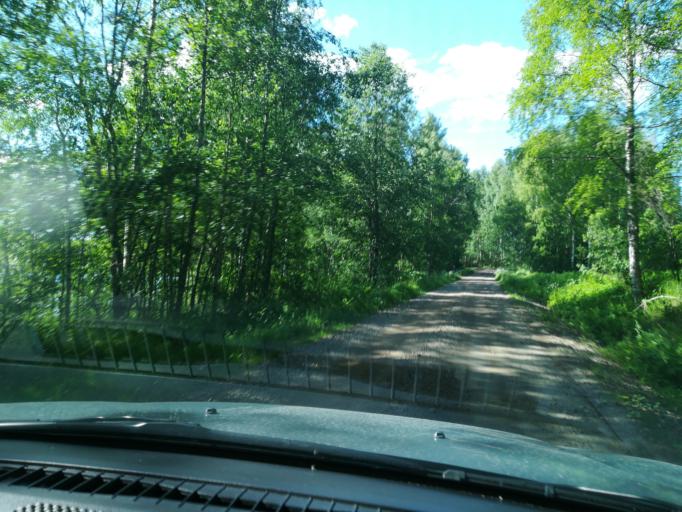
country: FI
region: Southern Savonia
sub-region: Mikkeli
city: Puumala
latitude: 61.6606
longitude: 28.1526
